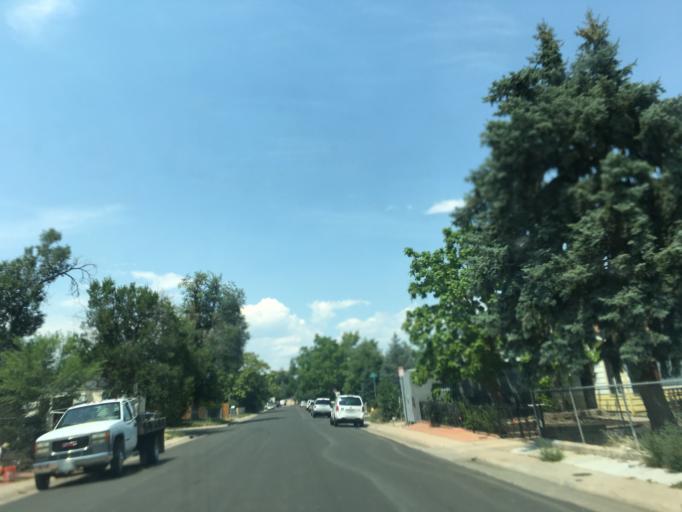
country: US
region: Colorado
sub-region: Jefferson County
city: Lakewood
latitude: 39.7058
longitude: -105.0318
